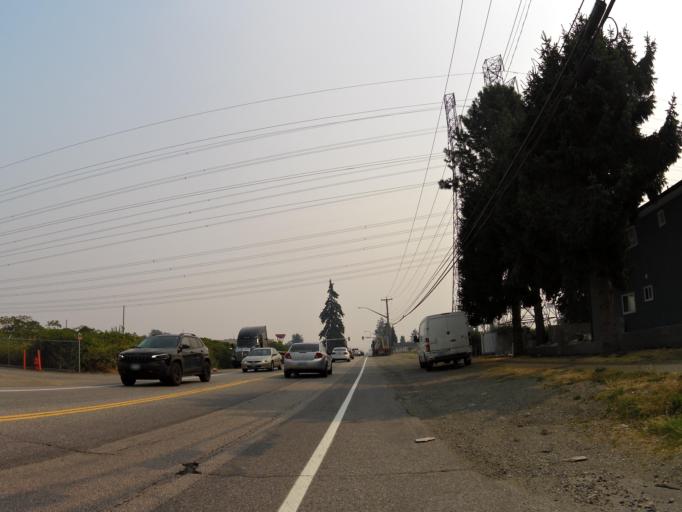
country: CA
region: British Columbia
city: Delta
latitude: 49.1483
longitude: -122.8755
